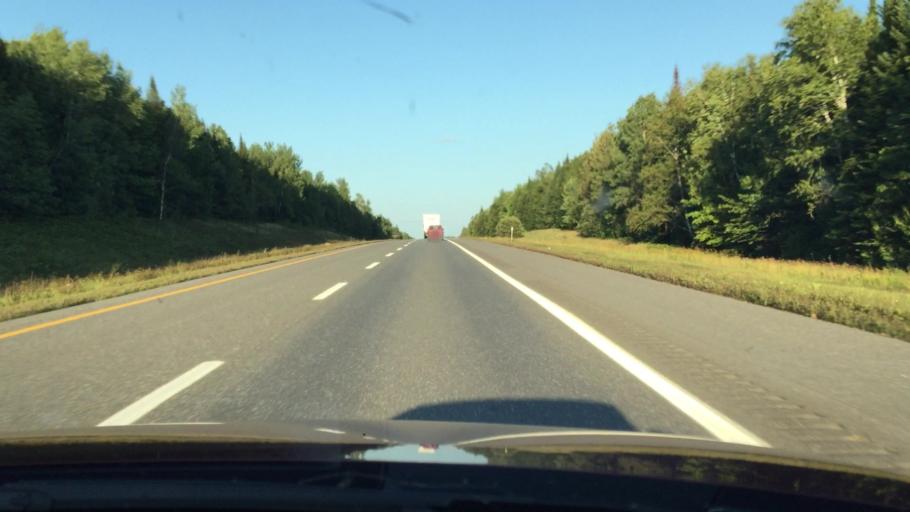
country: US
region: Maine
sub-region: Aroostook County
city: Hodgdon
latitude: 46.1399
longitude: -68.0081
